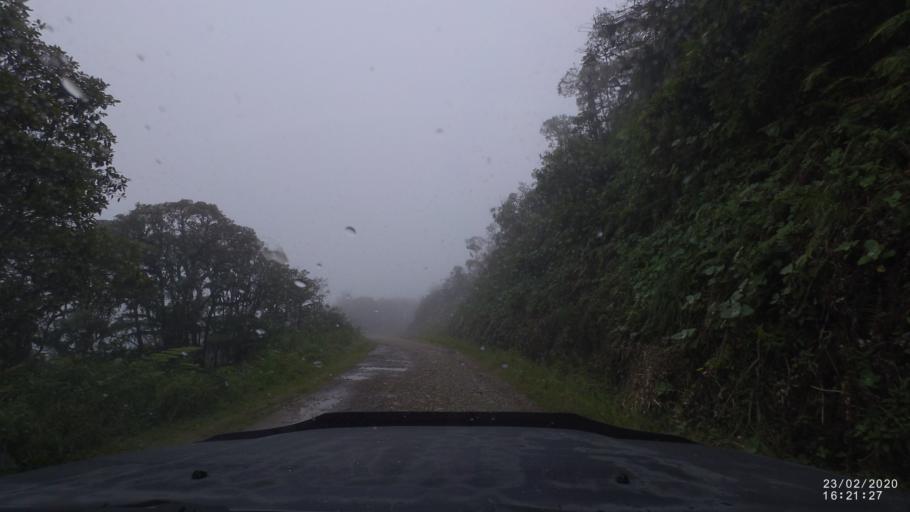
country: BO
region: Cochabamba
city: Colomi
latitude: -17.1124
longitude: -65.9674
